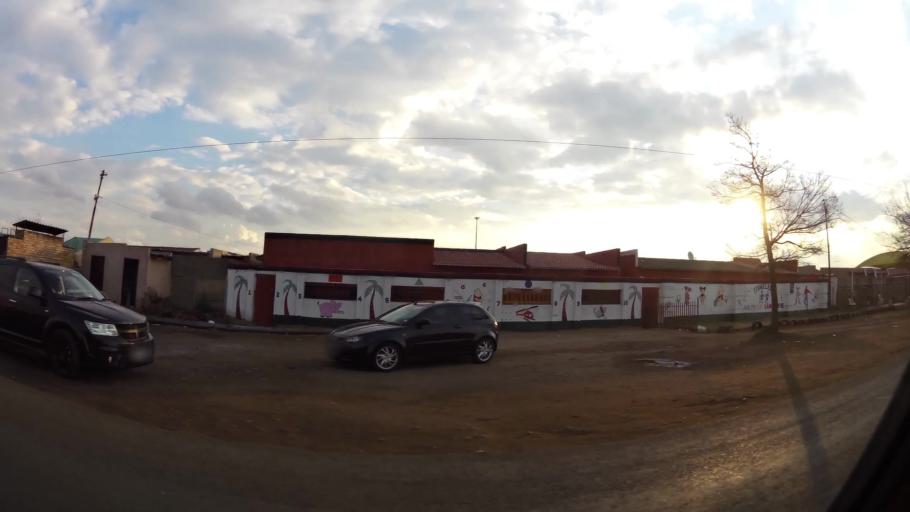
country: ZA
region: Gauteng
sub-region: City of Johannesburg Metropolitan Municipality
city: Orange Farm
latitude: -26.5894
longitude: 27.8468
